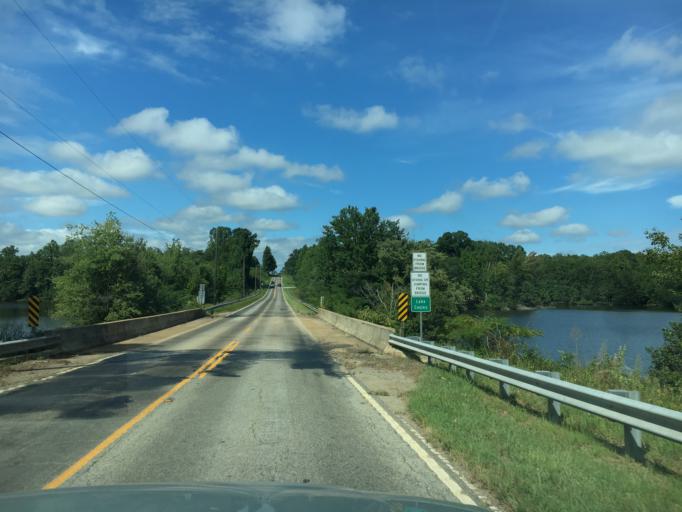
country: US
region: South Carolina
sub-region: Spartanburg County
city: Inman Mills
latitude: 35.0043
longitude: -82.1118
